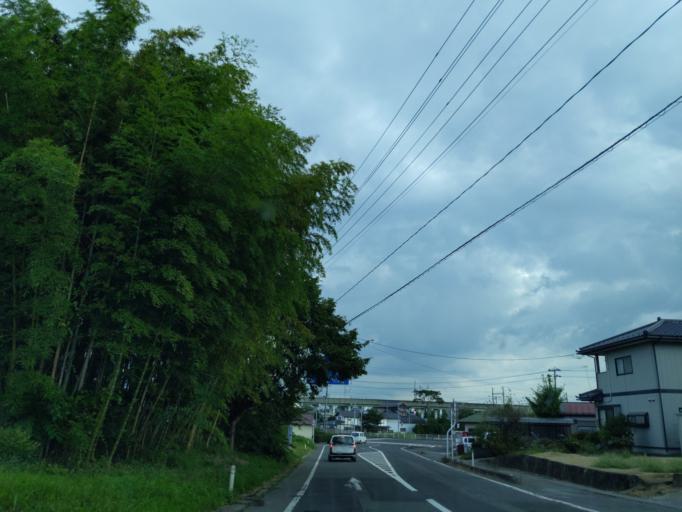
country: JP
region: Fukushima
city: Sukagawa
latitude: 37.3061
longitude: 140.3404
